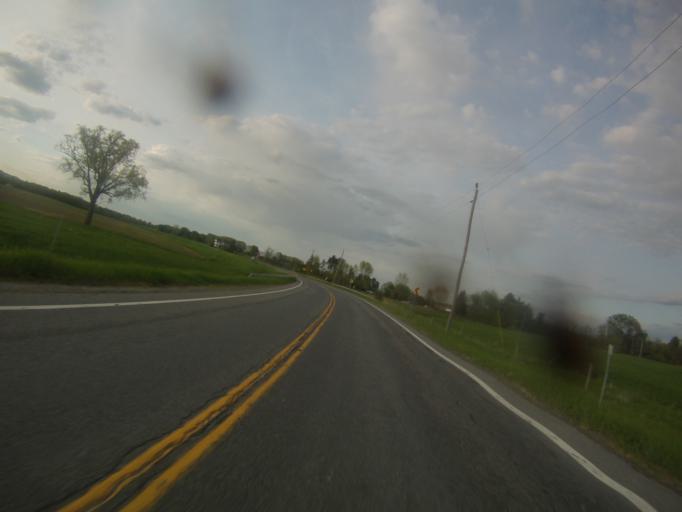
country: US
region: New York
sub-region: Essex County
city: Port Henry
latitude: 44.0002
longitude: -73.4203
